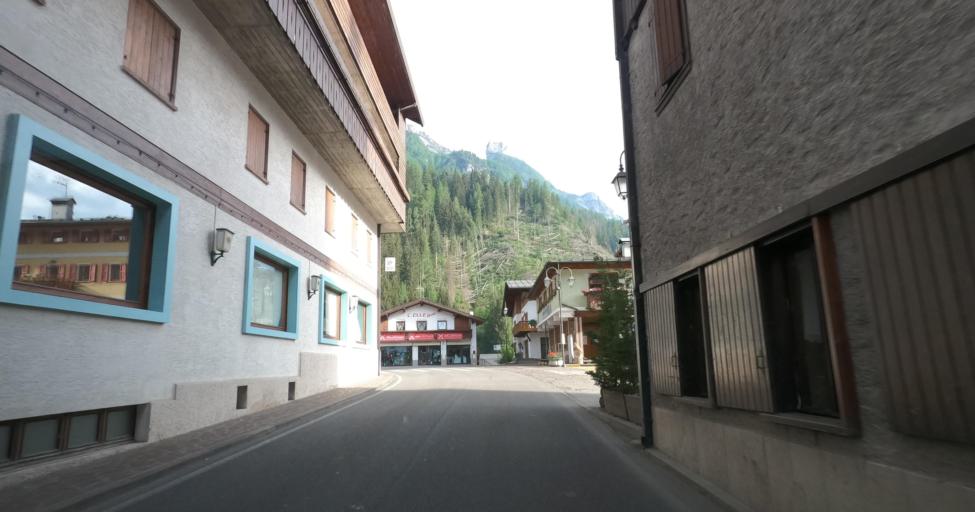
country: IT
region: Veneto
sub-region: Provincia di Belluno
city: Alleghe
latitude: 46.4064
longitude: 12.0205
